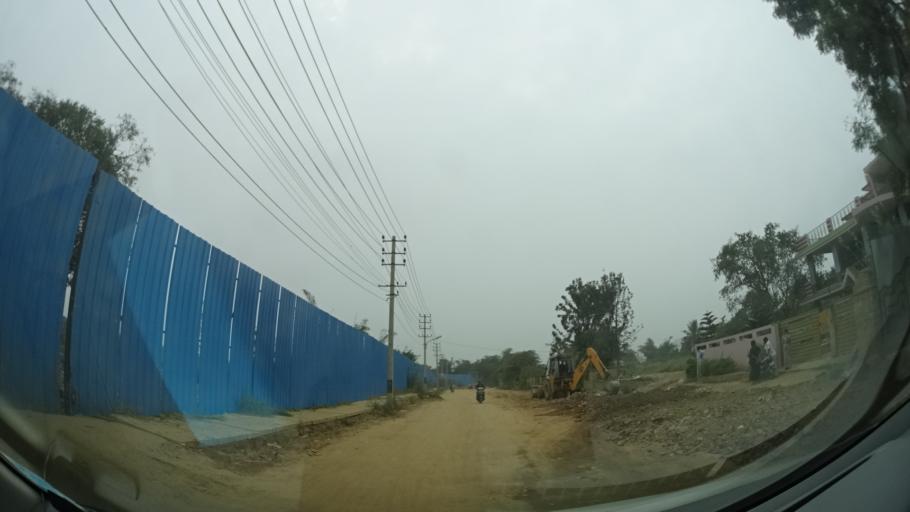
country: IN
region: Karnataka
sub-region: Bangalore Rural
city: Hoskote
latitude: 12.9670
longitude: 77.7429
